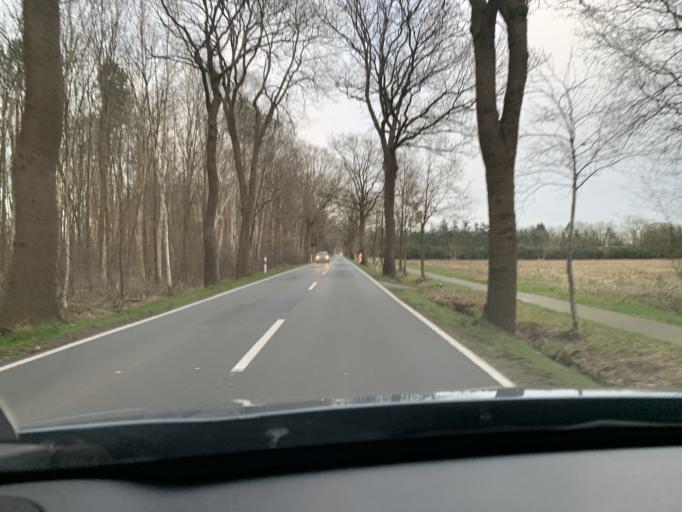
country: DE
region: Lower Saxony
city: Apen
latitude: 53.1787
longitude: 7.8337
